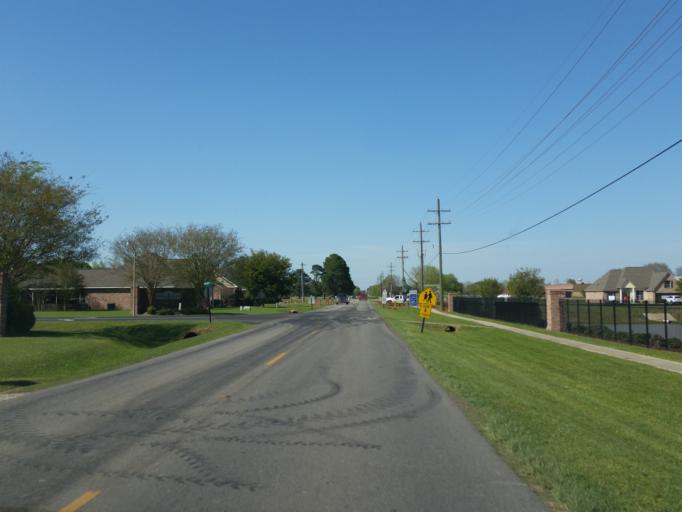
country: US
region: Louisiana
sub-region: Lafayette Parish
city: Broussard
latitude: 30.1220
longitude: -91.9652
